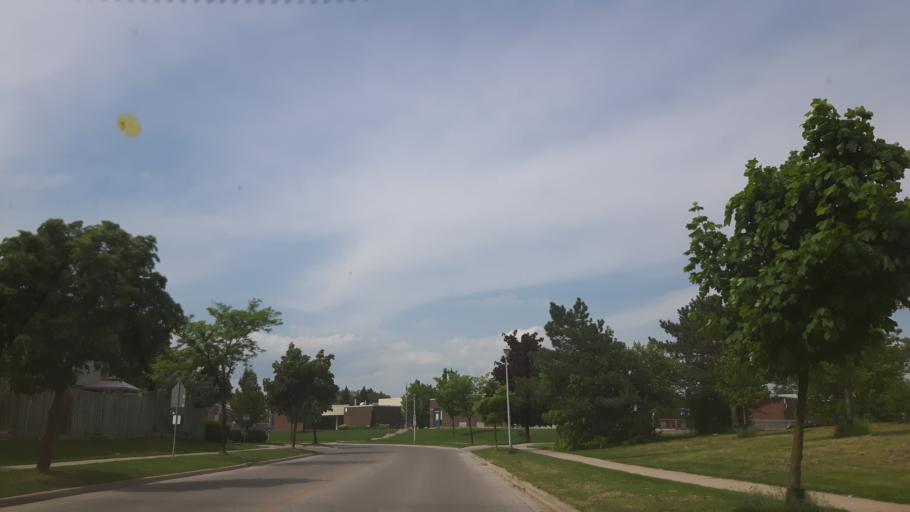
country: CA
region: Ontario
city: London
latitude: 42.9426
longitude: -81.2086
